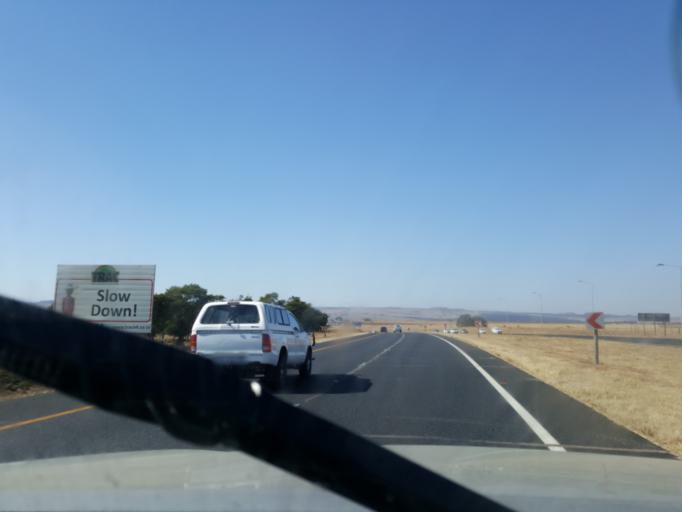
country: ZA
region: Mpumalanga
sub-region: Nkangala District Municipality
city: Witbank
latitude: -25.8758
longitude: 29.3468
